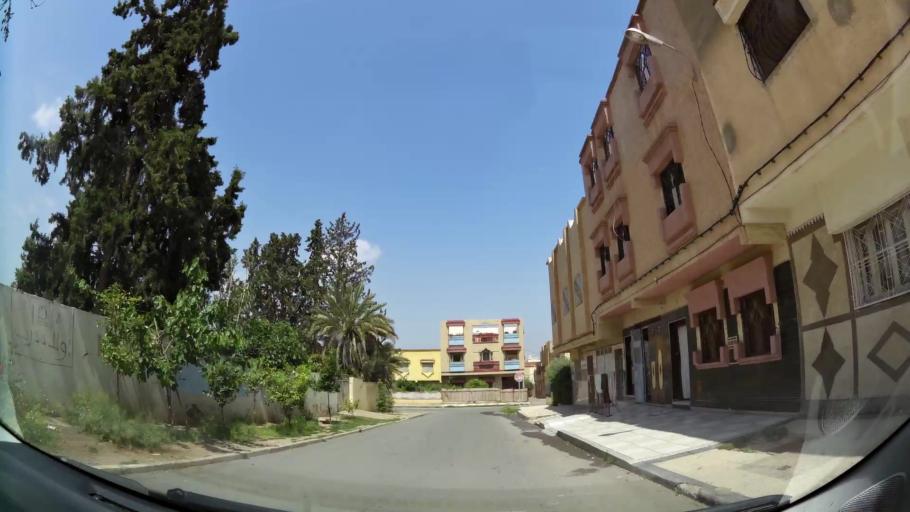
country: MA
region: Oriental
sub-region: Oujda-Angad
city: Oujda
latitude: 34.6866
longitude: -1.8841
